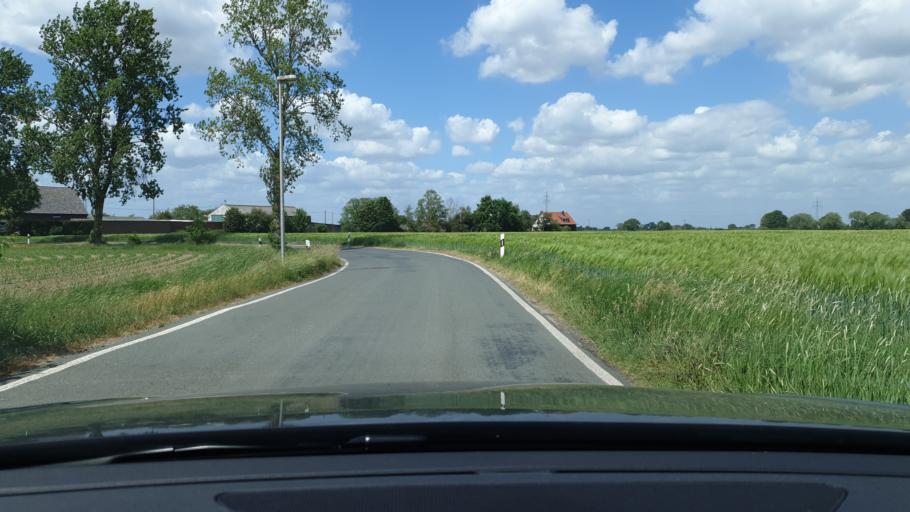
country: DE
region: North Rhine-Westphalia
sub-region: Regierungsbezirk Dusseldorf
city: Kleve
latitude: 51.8041
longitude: 6.0912
